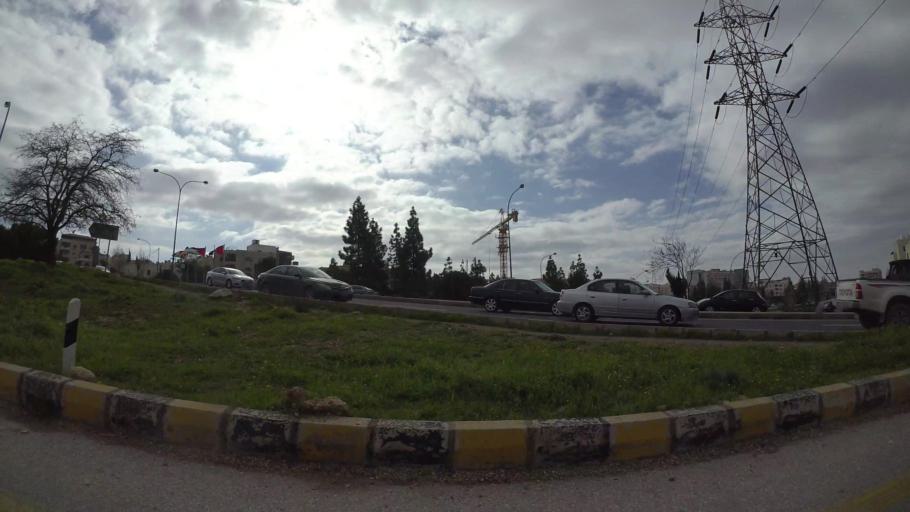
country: JO
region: Amman
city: Wadi as Sir
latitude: 31.9454
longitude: 35.8586
